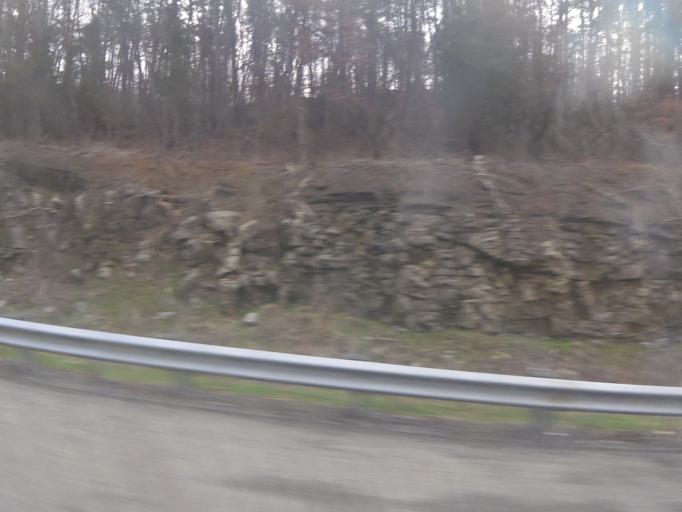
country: US
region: Georgia
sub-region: Walker County
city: Lookout Mountain
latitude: 34.9801
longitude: -85.4600
